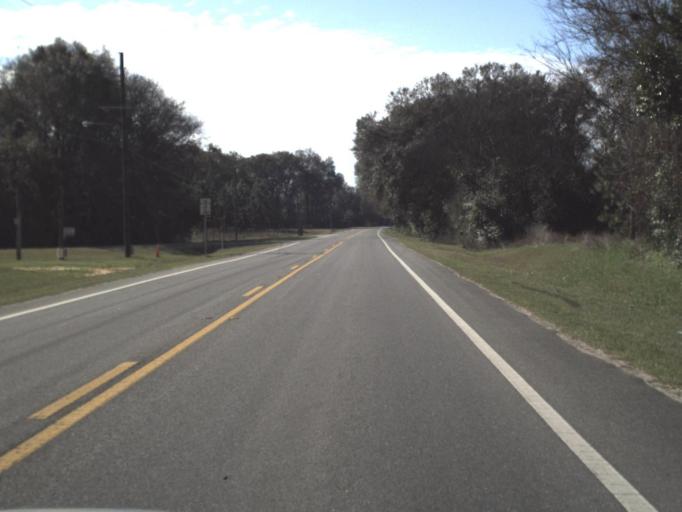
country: US
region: Florida
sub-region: Jackson County
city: Malone
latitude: 30.8807
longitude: -85.1614
